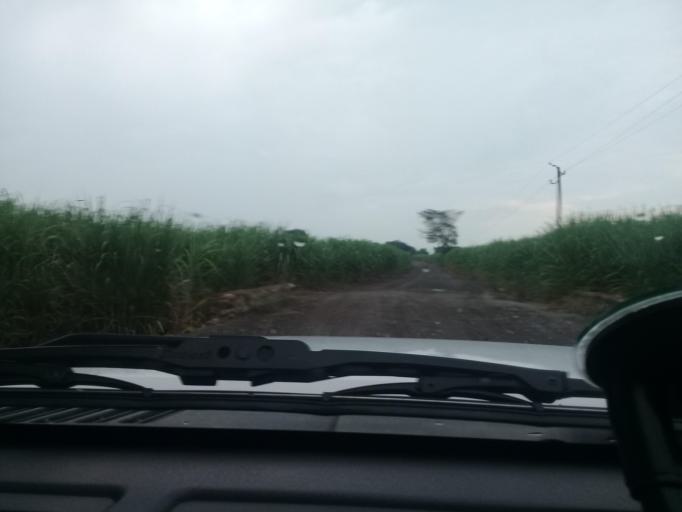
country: MX
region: Veracruz
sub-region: Puente Nacional
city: Cabezas
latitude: 19.3598
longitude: -96.4214
